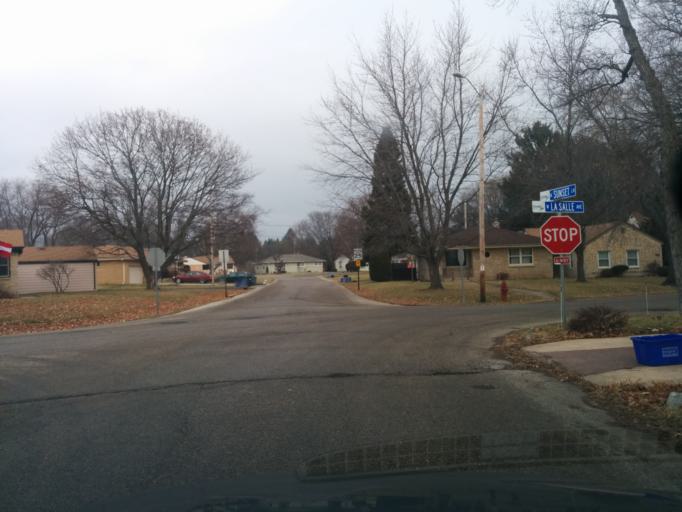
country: US
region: Wisconsin
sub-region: Milwaukee County
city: Glendale
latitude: 43.1218
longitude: -87.9218
